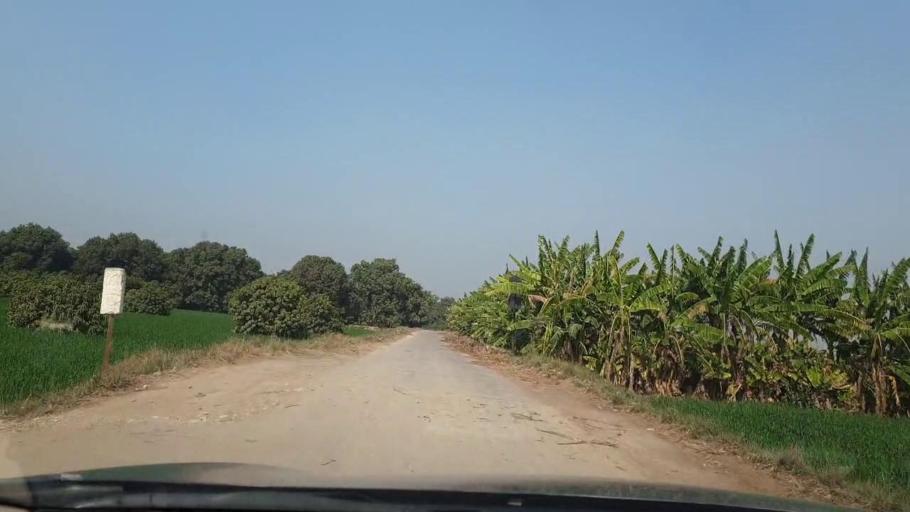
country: PK
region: Sindh
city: Tando Allahyar
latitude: 25.4840
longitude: 68.7917
